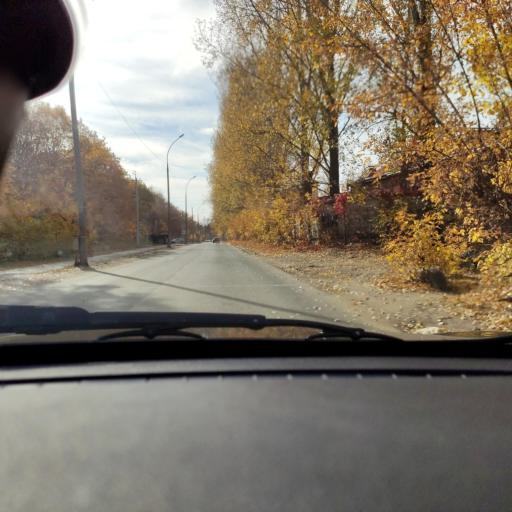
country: RU
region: Samara
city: Tol'yatti
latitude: 53.5047
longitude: 49.3050
